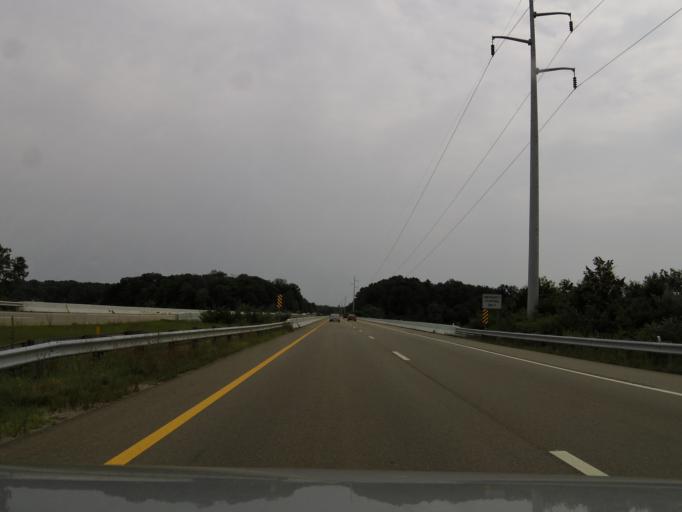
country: US
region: Ohio
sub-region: Warren County
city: Waynesville
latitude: 39.5087
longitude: -84.0252
